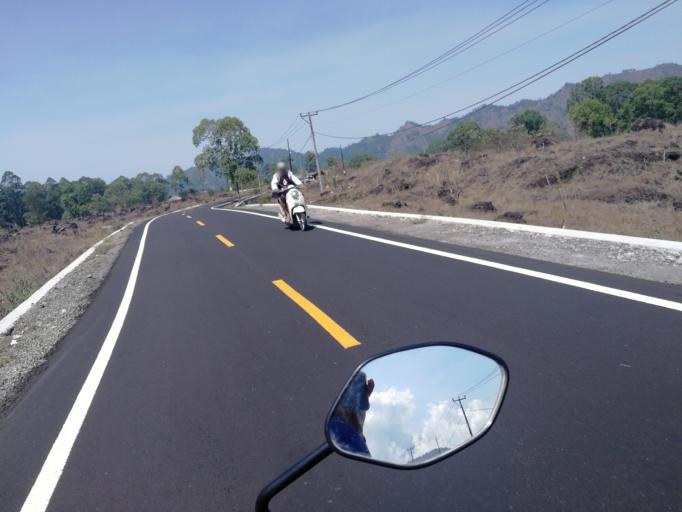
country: ID
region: Bali
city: Banjar Kedisan
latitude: -8.2556
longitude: 115.3951
